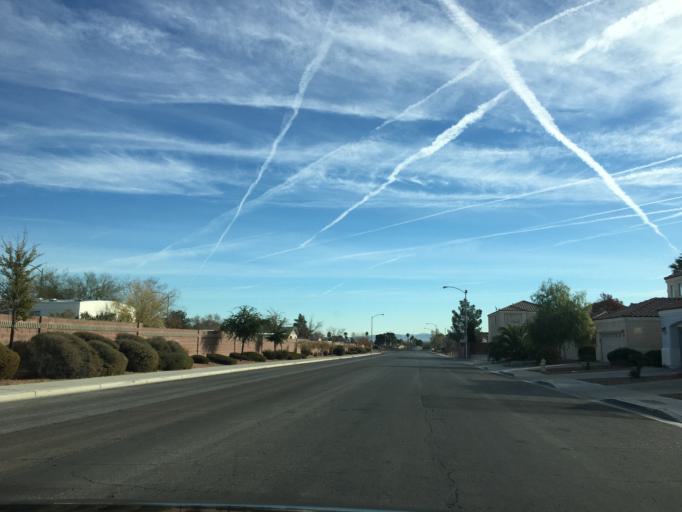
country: US
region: Nevada
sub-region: Clark County
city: Enterprise
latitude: 36.0173
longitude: -115.1757
